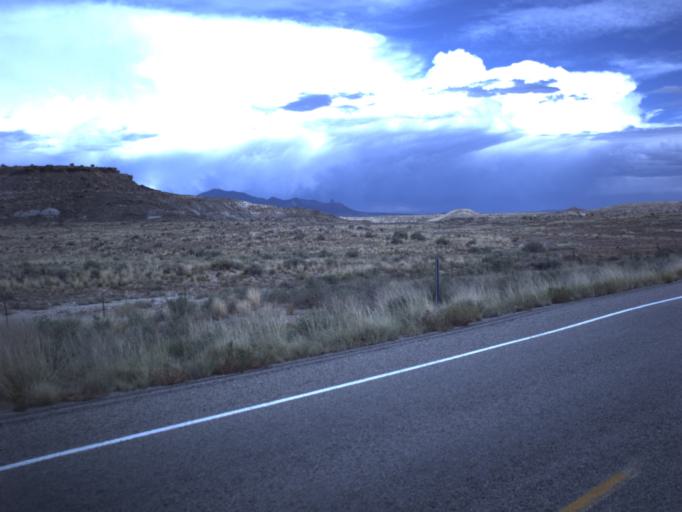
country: US
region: Colorado
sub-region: Montezuma County
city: Towaoc
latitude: 37.1583
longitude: -109.0604
